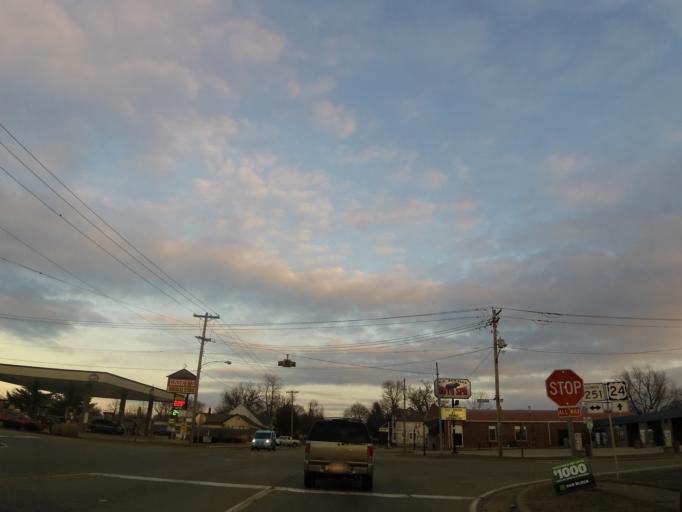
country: US
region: Illinois
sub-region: Woodford County
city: El Paso
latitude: 40.7370
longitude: -89.0252
